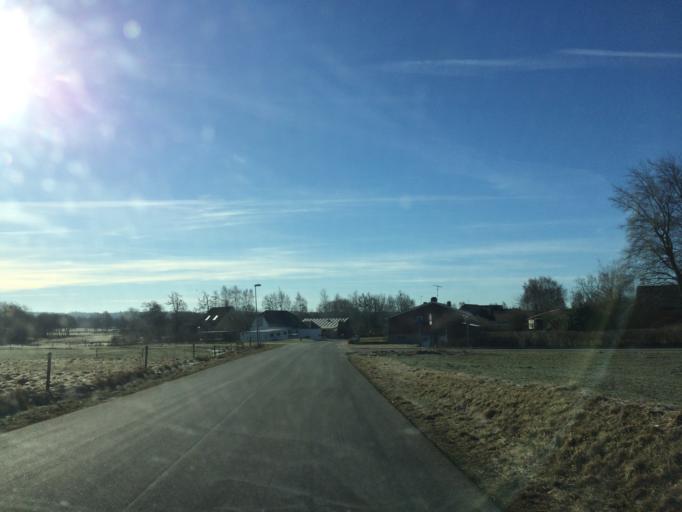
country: DK
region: North Denmark
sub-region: Mariagerfjord Kommune
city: Hobro
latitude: 56.5921
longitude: 9.6345
